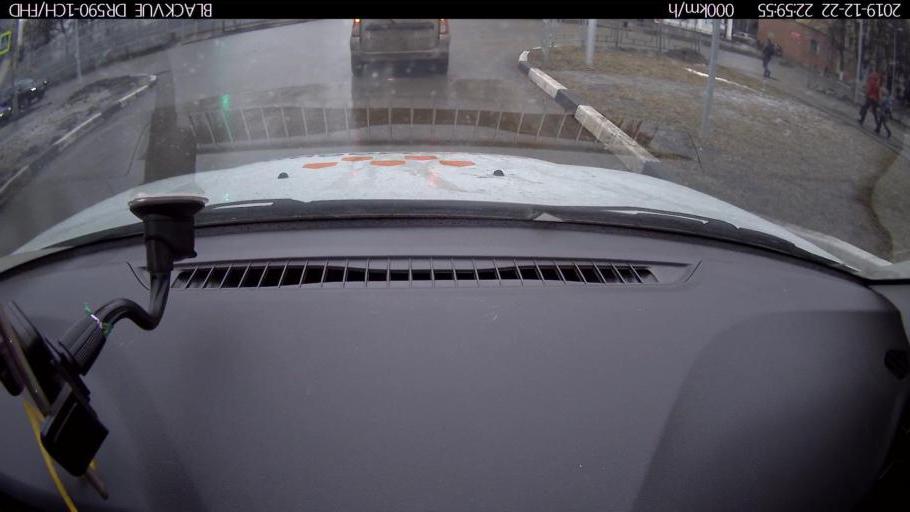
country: RU
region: Nizjnij Novgorod
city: Gorbatovka
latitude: 56.2431
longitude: 43.8459
